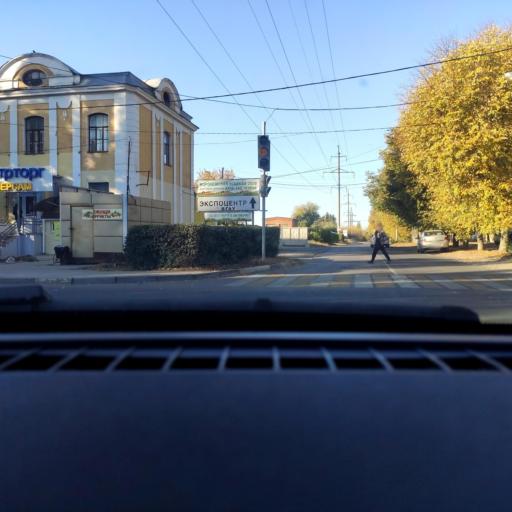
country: RU
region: Voronezj
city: Voronezh
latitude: 51.7141
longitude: 39.2237
